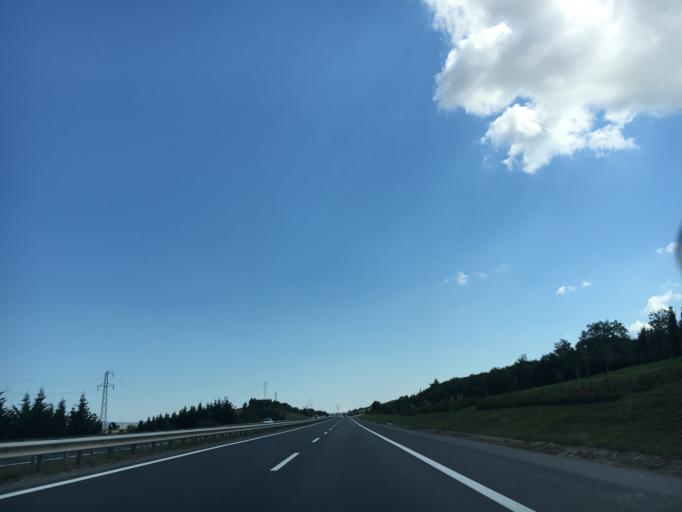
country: TR
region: Istanbul
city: Canta
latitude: 41.0806
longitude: 28.1294
